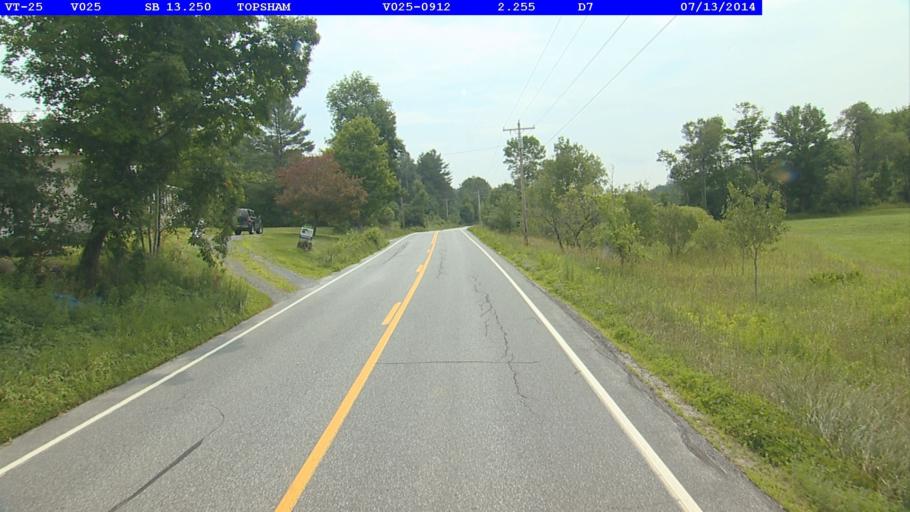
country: US
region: Vermont
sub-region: Orange County
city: Chelsea
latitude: 44.0970
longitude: -72.2969
